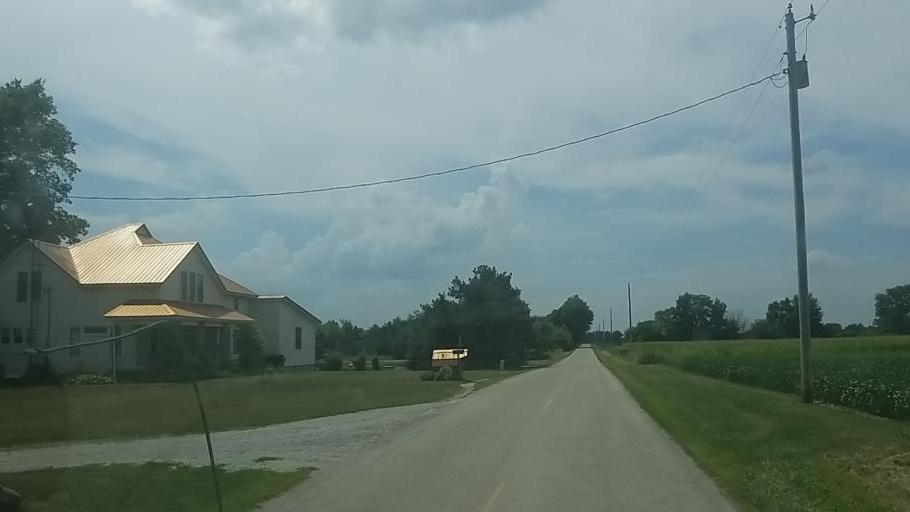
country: US
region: Ohio
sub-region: Hardin County
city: Kenton
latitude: 40.7394
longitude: -83.5945
